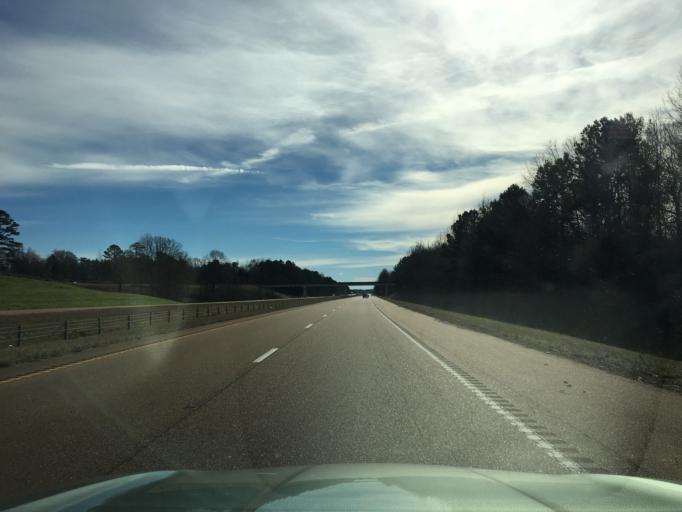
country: US
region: Mississippi
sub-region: Union County
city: New Albany
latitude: 34.4320
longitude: -88.9632
